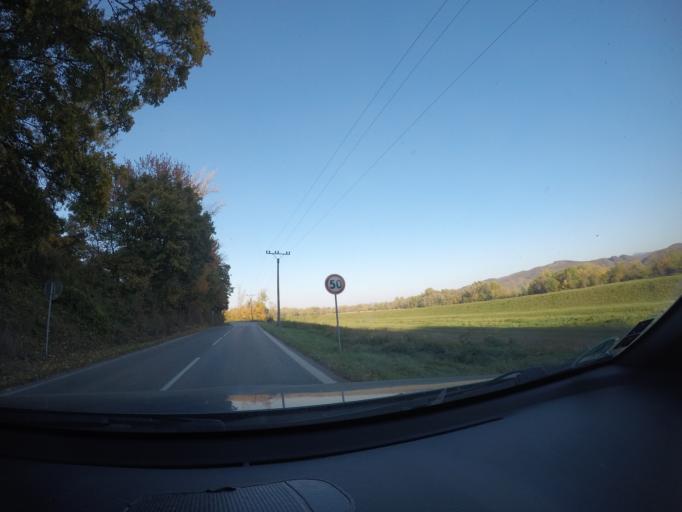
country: SK
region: Trenciansky
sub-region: Okres Trencin
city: Trencin
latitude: 48.9201
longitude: 18.0754
